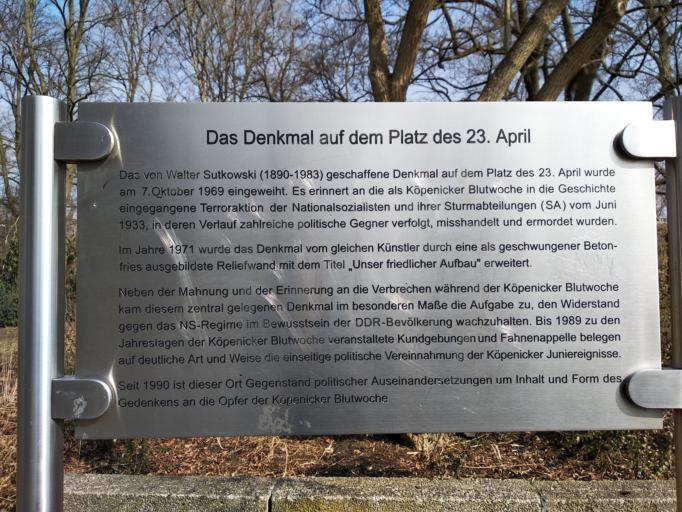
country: DE
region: Berlin
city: Kopenick Bezirk
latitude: 52.4512
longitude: 13.5737
